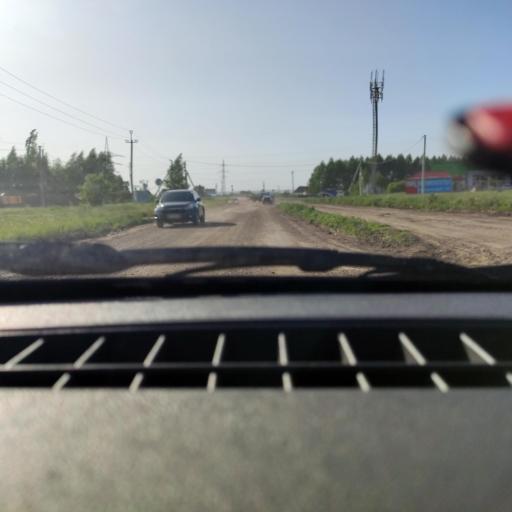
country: RU
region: Bashkortostan
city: Iglino
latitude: 54.8203
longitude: 56.4230
